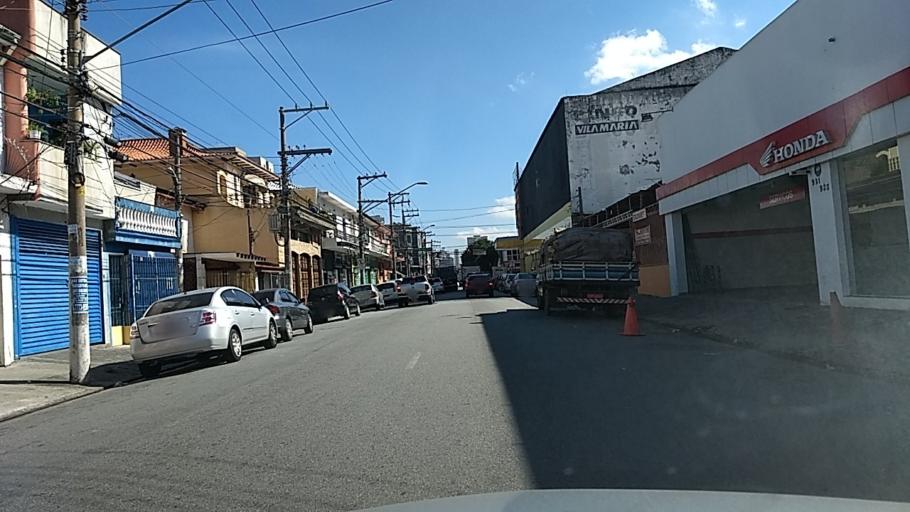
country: BR
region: Sao Paulo
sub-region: Sao Paulo
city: Sao Paulo
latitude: -23.5144
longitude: -46.5854
